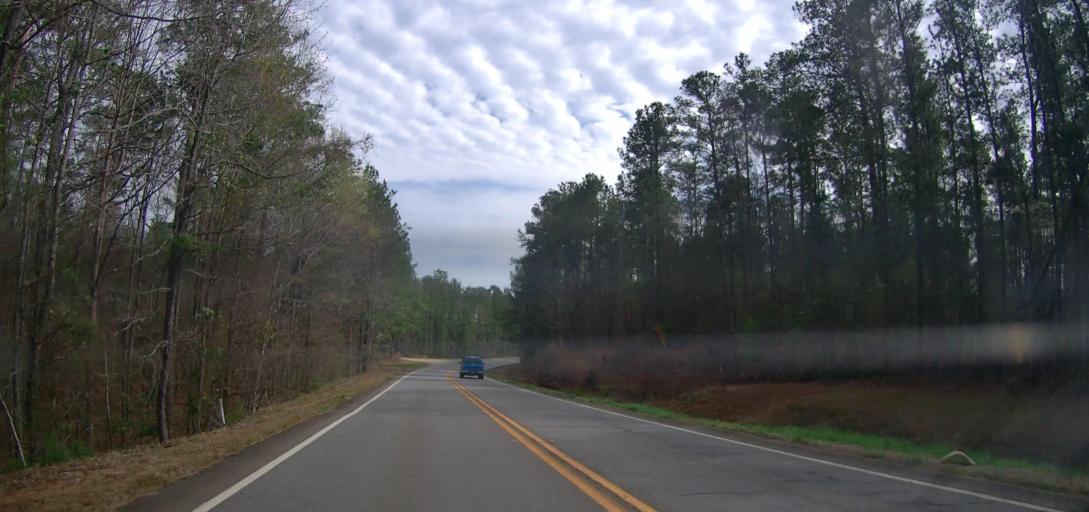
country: US
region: Georgia
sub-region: Jones County
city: Gray
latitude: 33.0142
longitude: -83.7028
